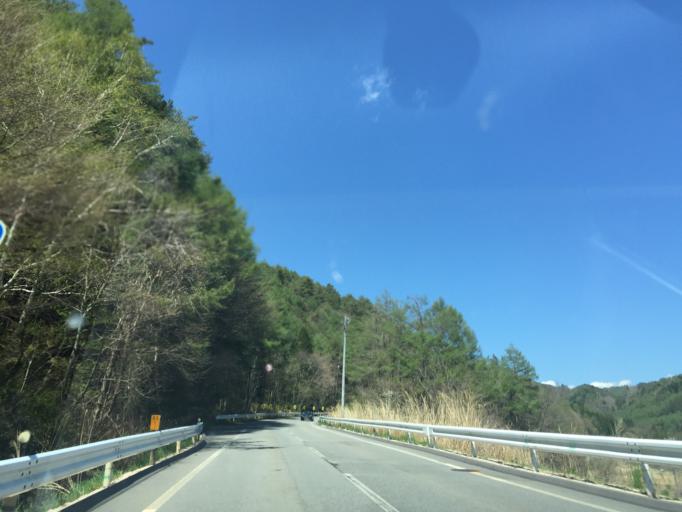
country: JP
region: Gifu
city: Nakatsugawa
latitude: 35.3320
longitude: 137.6436
